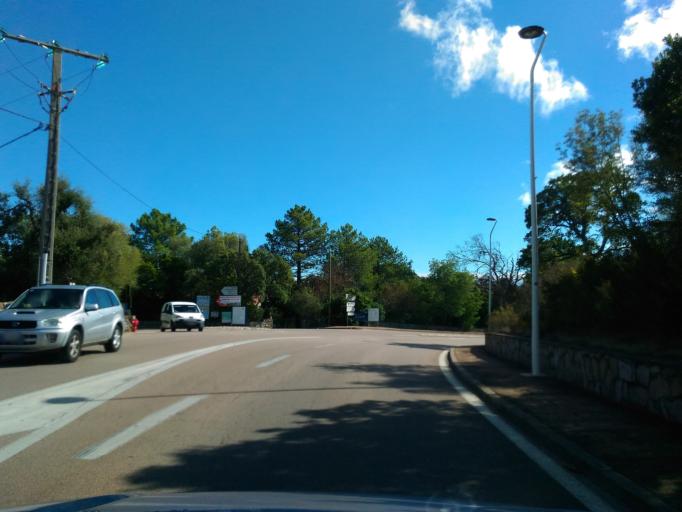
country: FR
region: Corsica
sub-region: Departement de la Corse-du-Sud
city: Porto-Vecchio
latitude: 41.6976
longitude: 9.3560
